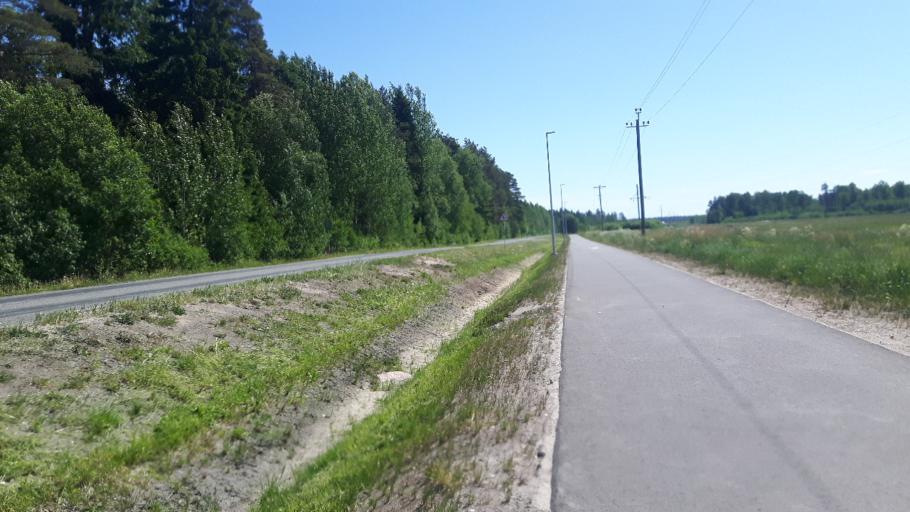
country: EE
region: Raplamaa
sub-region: Kohila vald
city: Kohila
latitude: 59.2118
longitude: 24.6817
